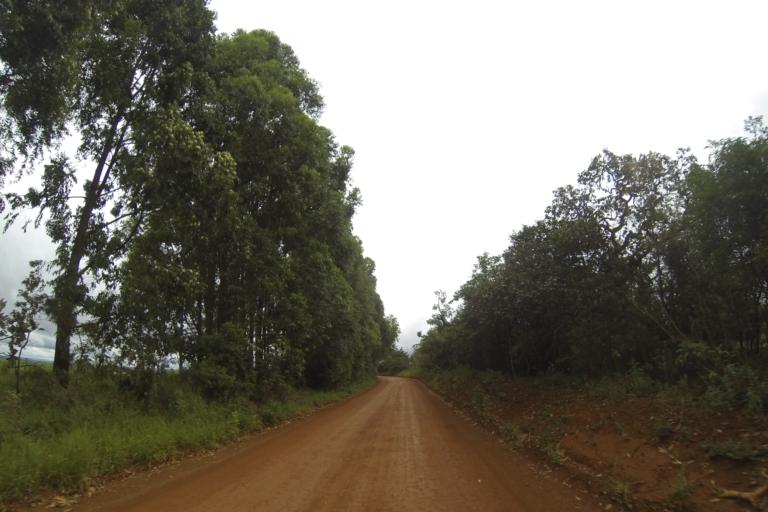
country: BR
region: Minas Gerais
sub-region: Campos Altos
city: Campos Altos
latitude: -19.8539
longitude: -46.3175
